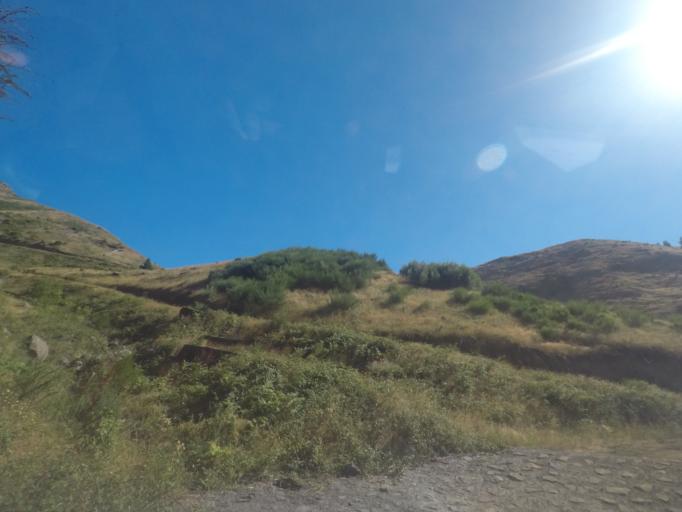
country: PT
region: Madeira
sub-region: Funchal
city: Nossa Senhora do Monte
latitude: 32.7082
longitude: -16.9028
